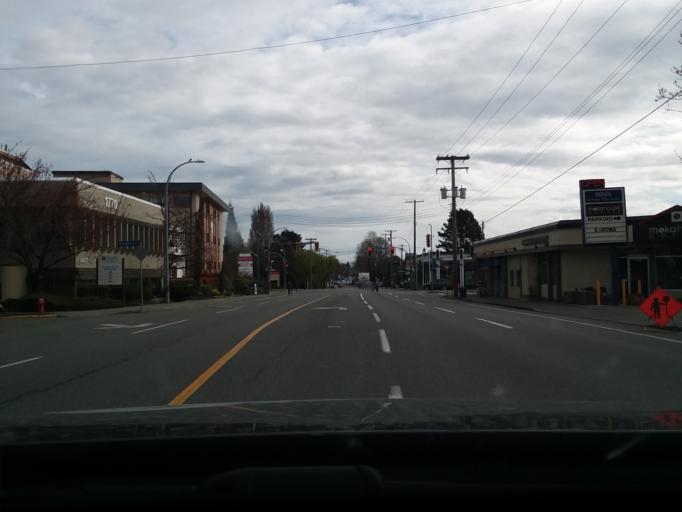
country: CA
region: British Columbia
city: Oak Bay
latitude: 48.4291
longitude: -123.3312
